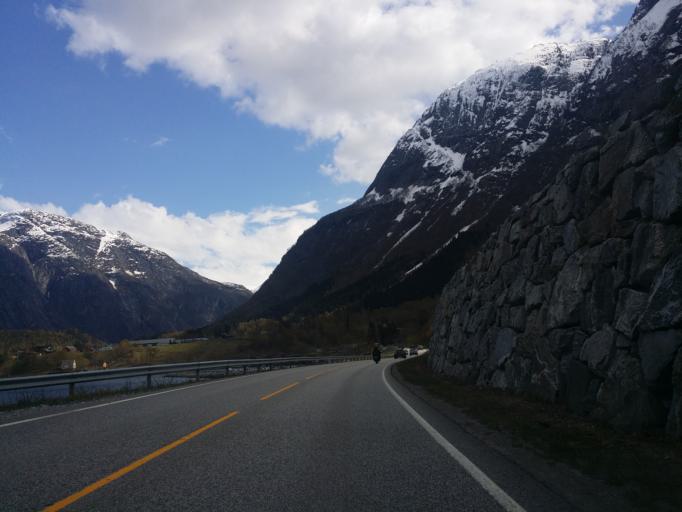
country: NO
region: Hordaland
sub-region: Eidfjord
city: Eidfjord
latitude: 60.4667
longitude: 7.0537
